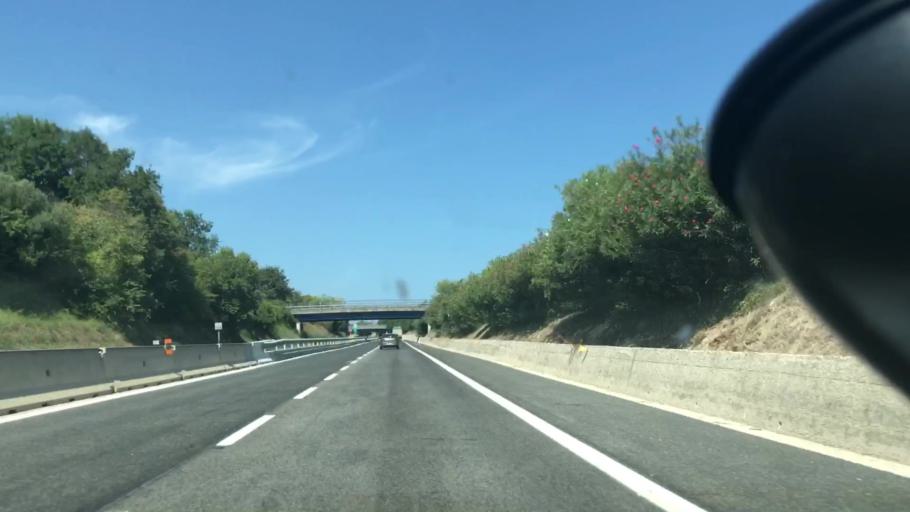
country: IT
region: Abruzzo
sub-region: Provincia di Chieti
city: Casalbordino-Miracoli
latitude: 42.1663
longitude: 14.6276
